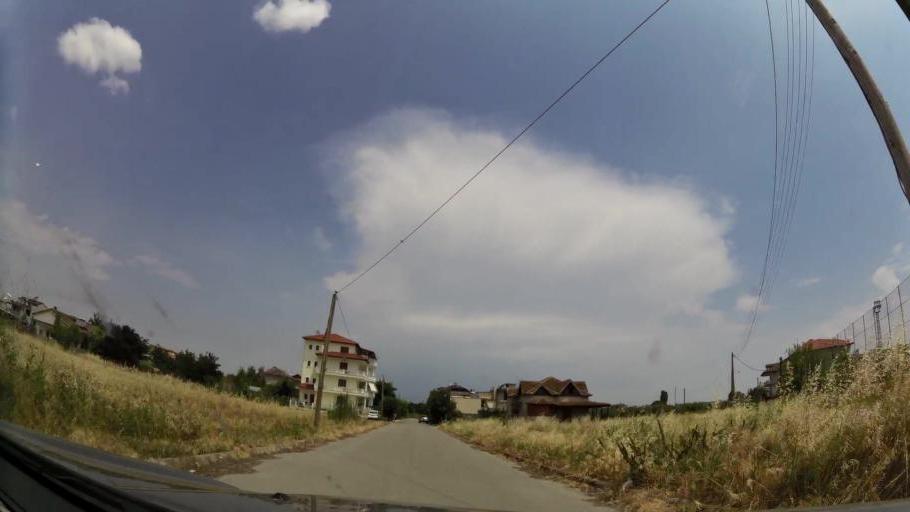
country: GR
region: Central Macedonia
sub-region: Nomos Pierias
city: Peristasi
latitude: 40.2747
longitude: 22.5451
